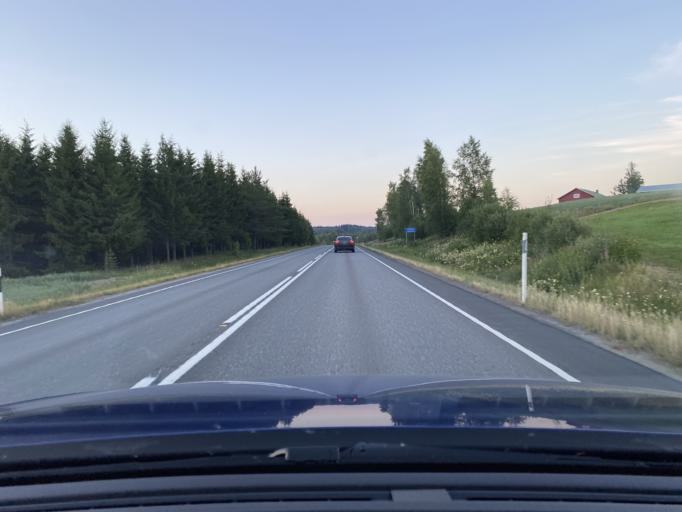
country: FI
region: Pirkanmaa
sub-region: Luoteis-Pirkanmaa
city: Ikaalinen
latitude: 61.8614
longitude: 22.9545
